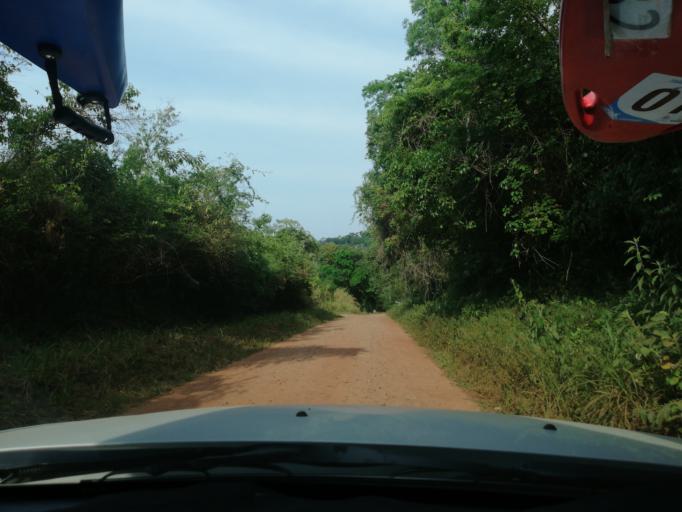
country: AR
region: Misiones
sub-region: Departamento de San Ignacio
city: San Ignacio
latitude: -27.2936
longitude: -55.5657
